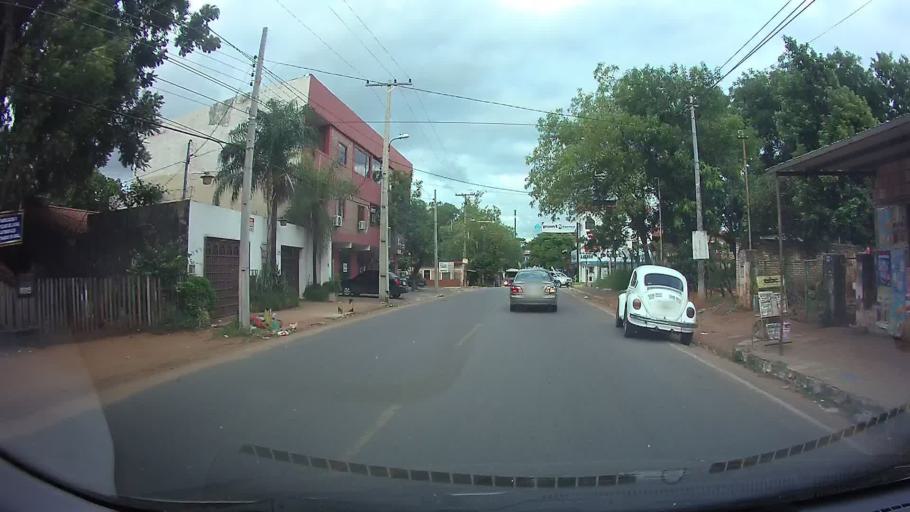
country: PY
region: Central
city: Fernando de la Mora
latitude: -25.3091
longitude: -57.5293
